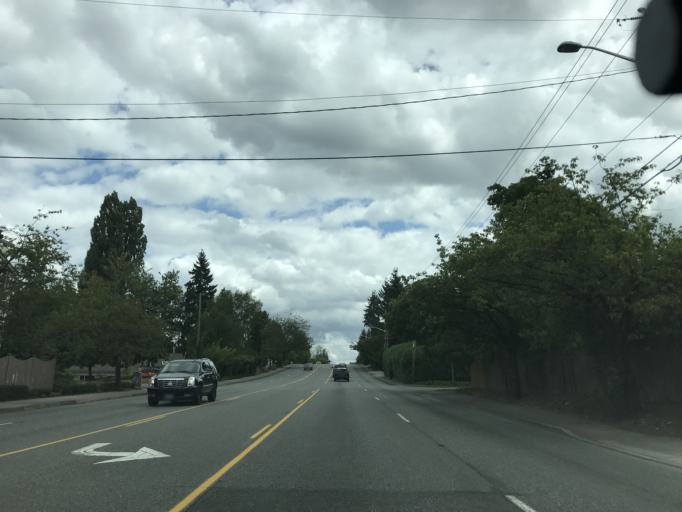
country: US
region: Washington
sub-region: King County
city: Fairwood
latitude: 47.4452
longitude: -122.1930
